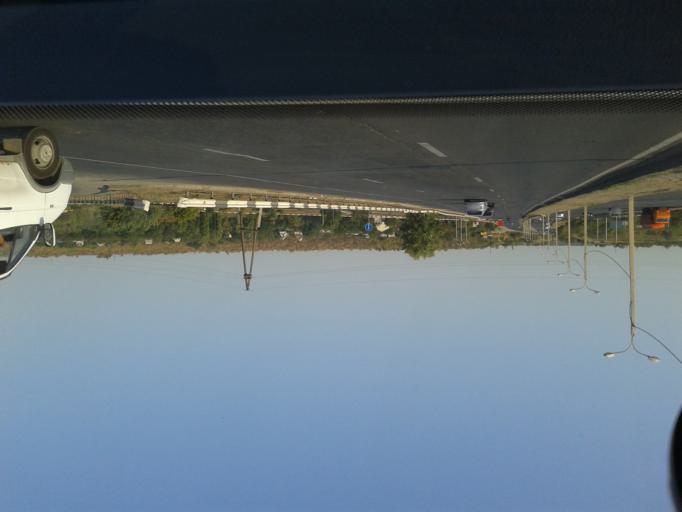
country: RU
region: Volgograd
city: Volgograd
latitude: 48.7336
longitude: 44.4554
